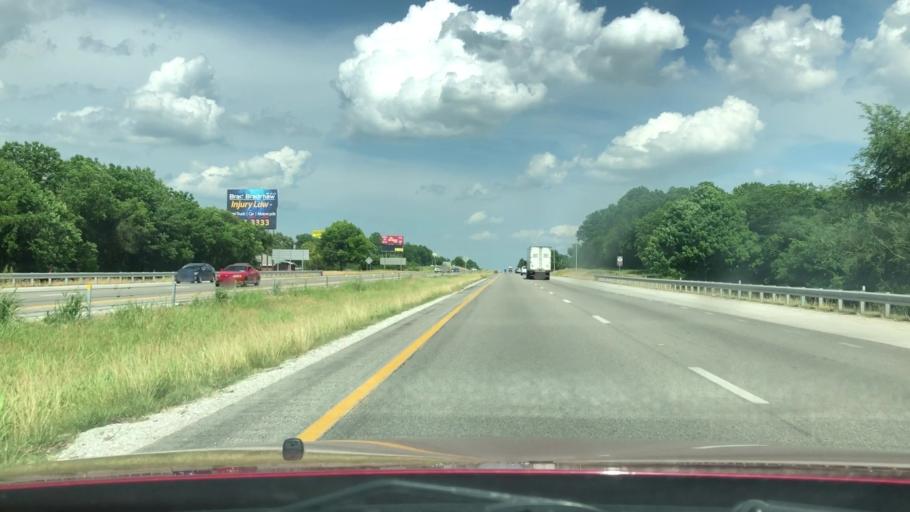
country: US
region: Missouri
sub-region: Greene County
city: Springfield
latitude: 37.2502
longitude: -93.3061
